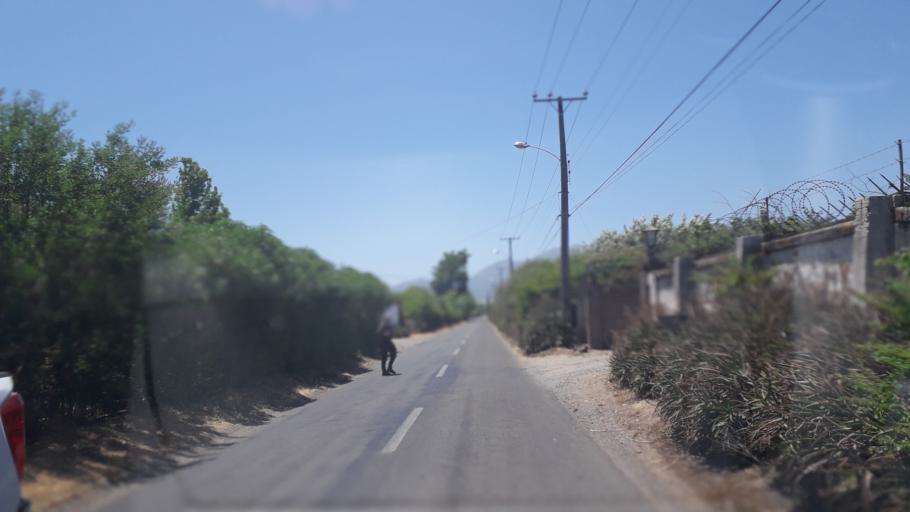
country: CL
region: Valparaiso
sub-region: Provincia de Quillota
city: Quillota
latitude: -32.9243
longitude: -71.2466
